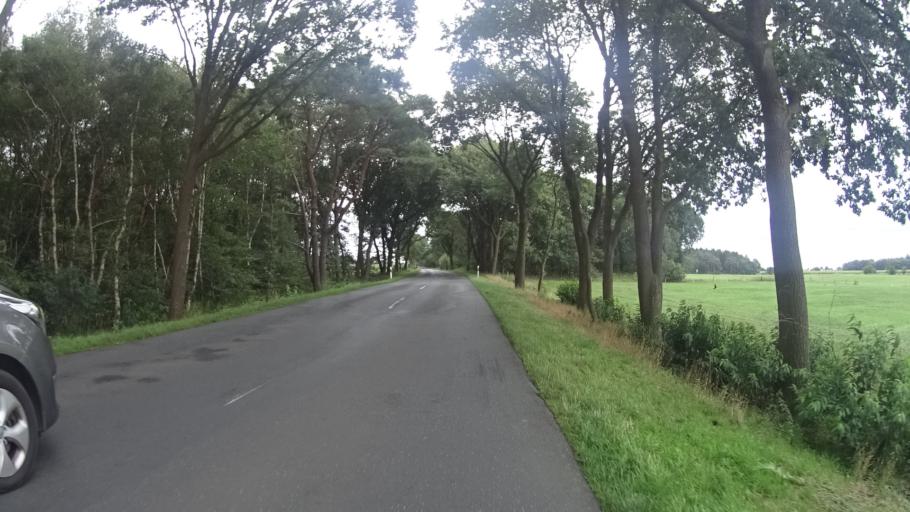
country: DE
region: Lower Saxony
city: Elmlohe
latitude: 53.5789
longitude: 8.7690
